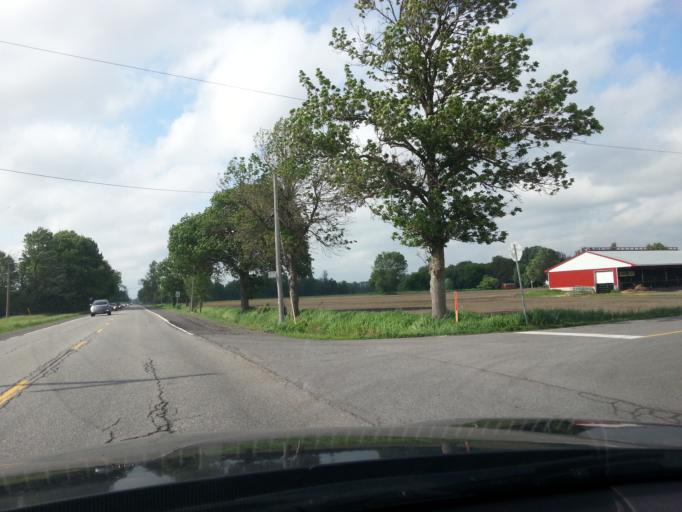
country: CA
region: Ontario
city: Bells Corners
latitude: 45.2343
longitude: -75.8103
